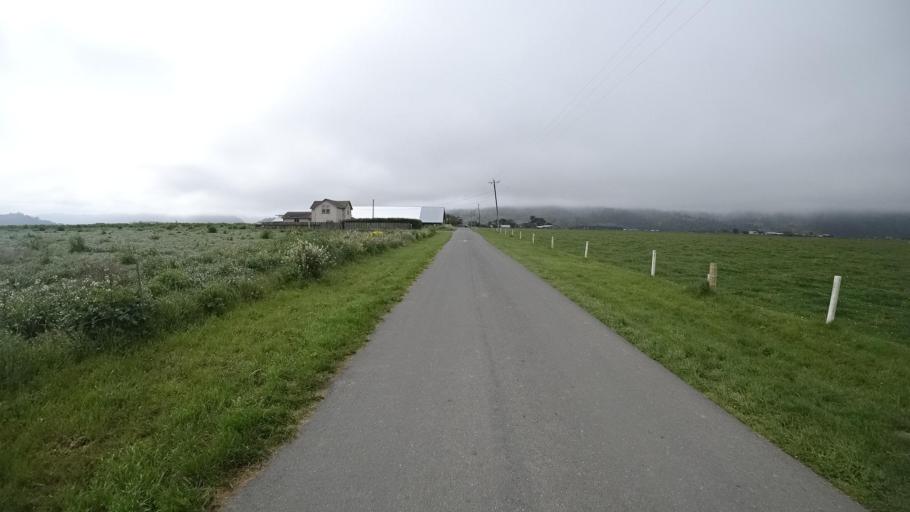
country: US
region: California
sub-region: Humboldt County
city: Fortuna
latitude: 40.5730
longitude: -124.1878
